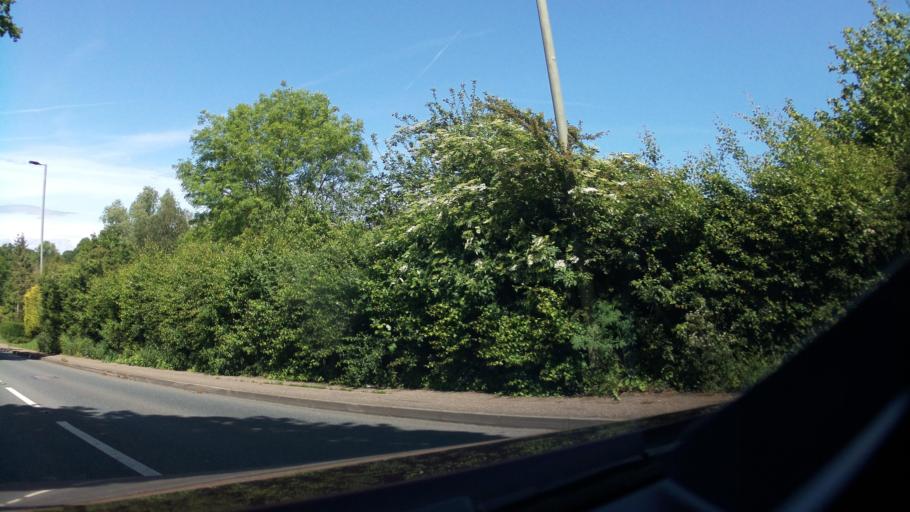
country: GB
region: England
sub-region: Devon
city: Exmouth
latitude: 50.6450
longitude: -3.4139
